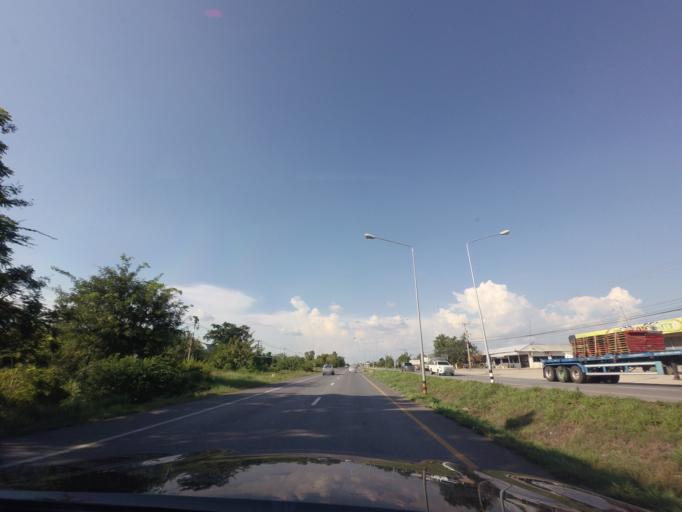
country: TH
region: Khon Kaen
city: Non Sila
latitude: 15.9819
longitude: 102.6961
